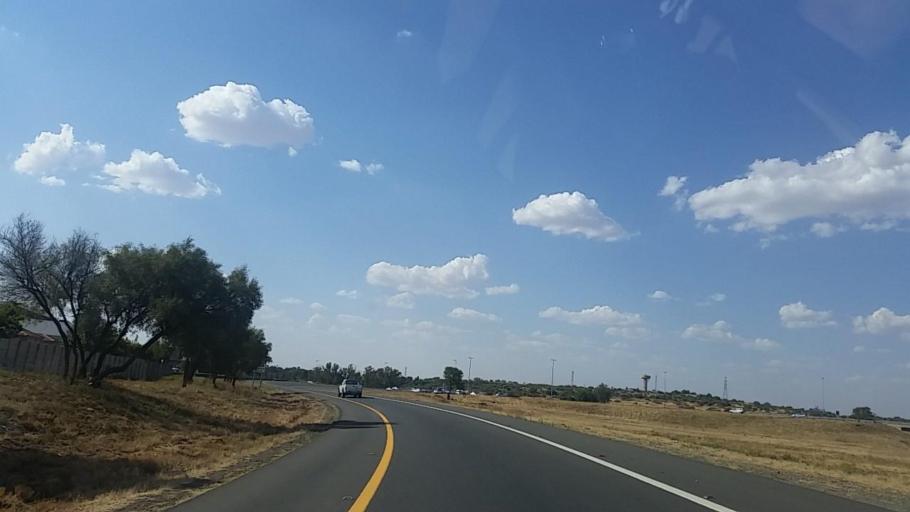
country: ZA
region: Orange Free State
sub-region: Mangaung Metropolitan Municipality
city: Bloemfontein
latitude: -29.0921
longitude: 26.1693
